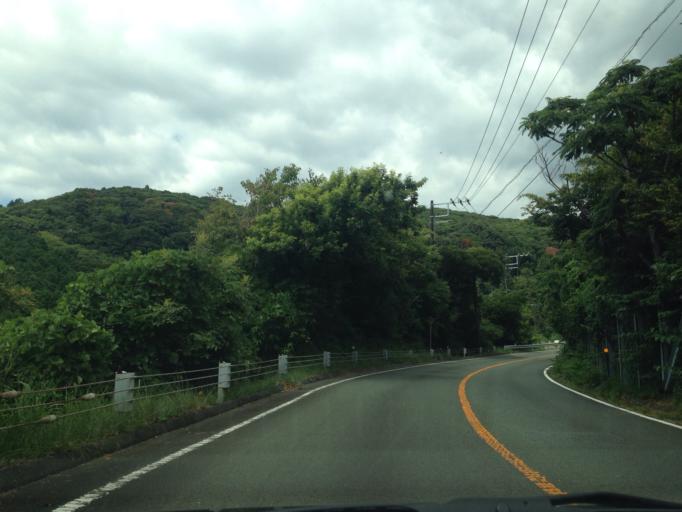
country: JP
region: Shizuoka
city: Shimoda
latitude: 34.6777
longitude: 138.7805
